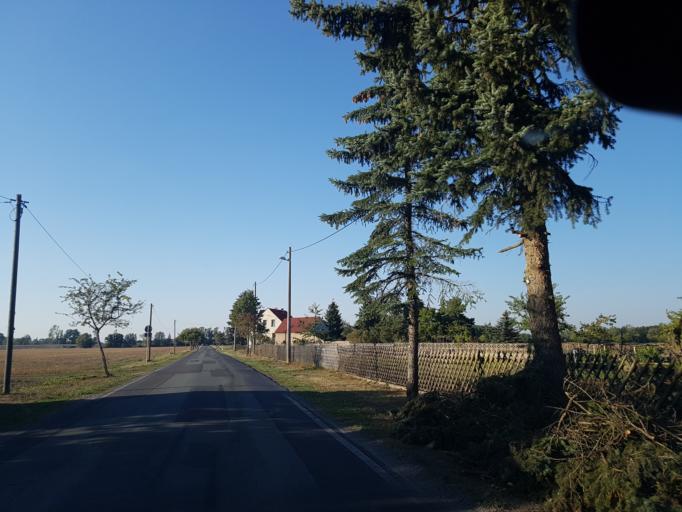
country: DE
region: Brandenburg
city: Bad Liebenwerda
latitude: 51.4966
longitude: 13.4074
